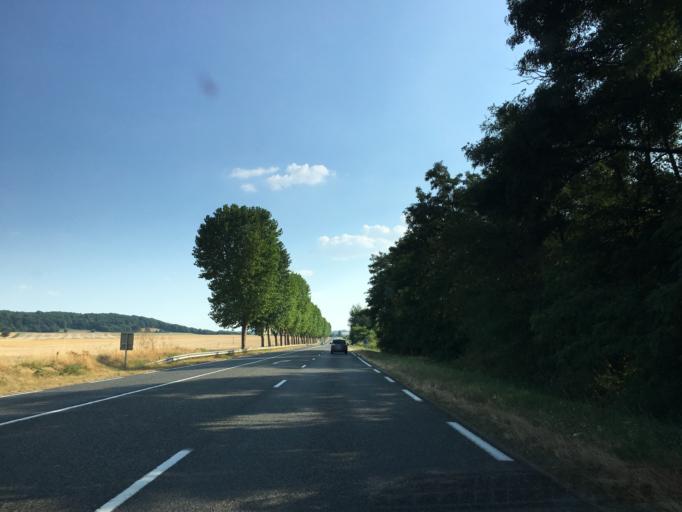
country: FR
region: Bourgogne
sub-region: Departement de l'Yonne
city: Veron
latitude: 48.1192
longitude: 3.2910
